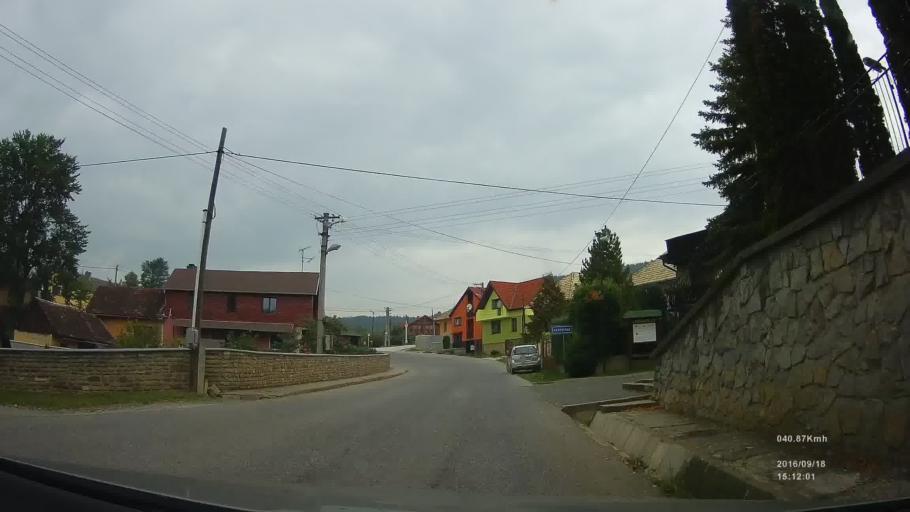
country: SK
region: Presovsky
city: Lubica
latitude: 49.0194
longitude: 20.4854
